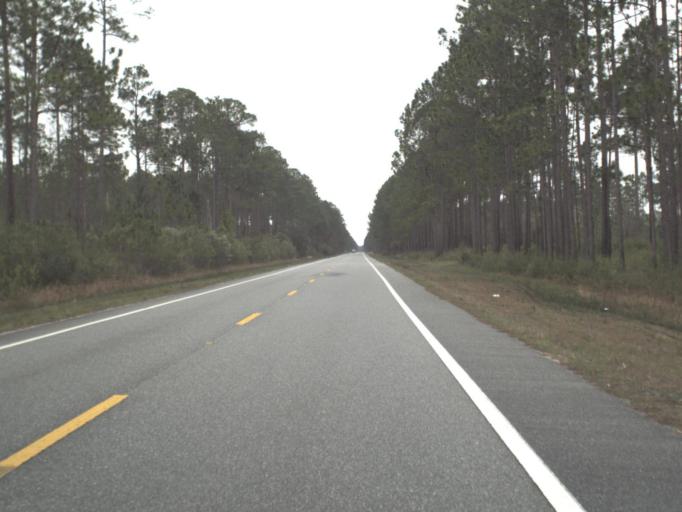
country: US
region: Florida
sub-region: Franklin County
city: Apalachicola
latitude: 29.8911
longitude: -84.9774
